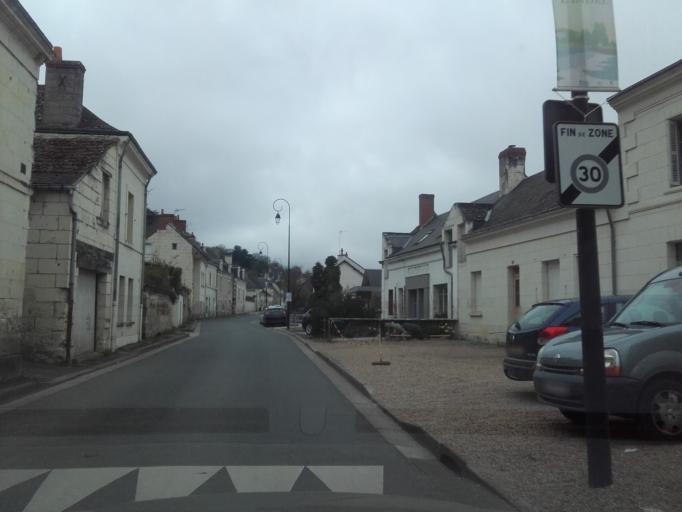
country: FR
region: Centre
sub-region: Departement d'Indre-et-Loire
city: Huismes
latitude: 47.2521
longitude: 0.2984
